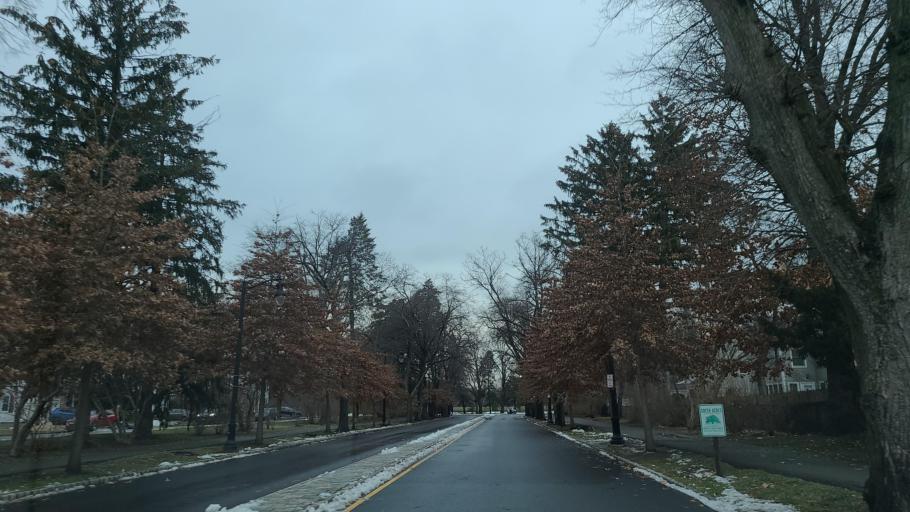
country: US
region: New Jersey
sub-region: Essex County
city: Brookdale
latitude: 40.8287
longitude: -74.1882
